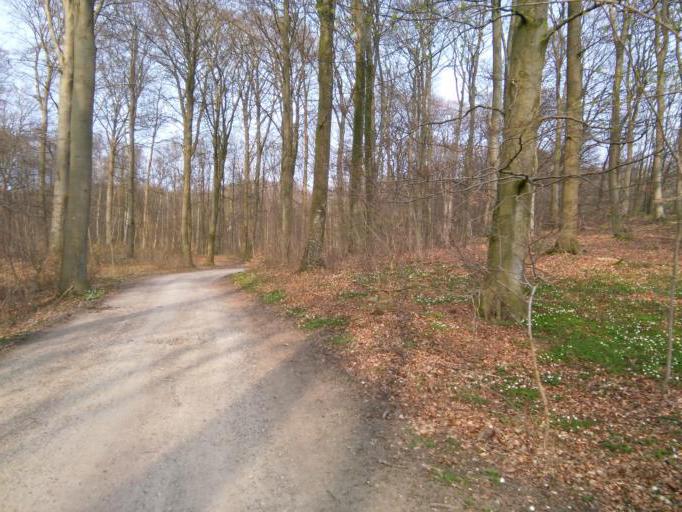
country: DK
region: Central Jutland
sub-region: Arhus Kommune
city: Beder
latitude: 56.0817
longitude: 10.2372
